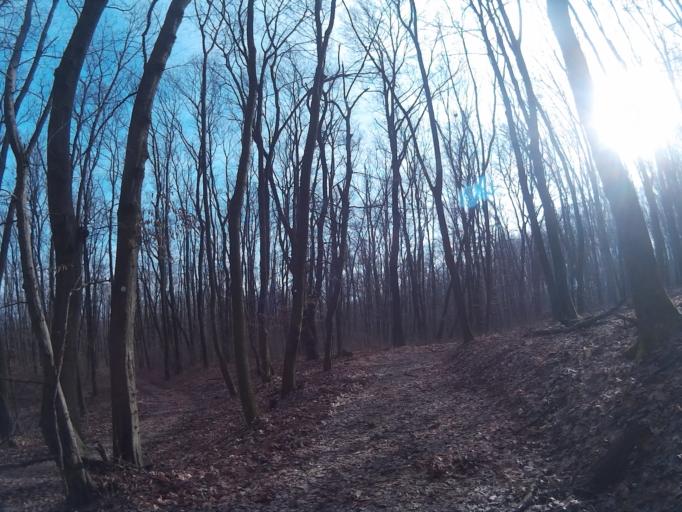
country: HU
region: Komarom-Esztergom
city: Tarjan
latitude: 47.6090
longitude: 18.4770
